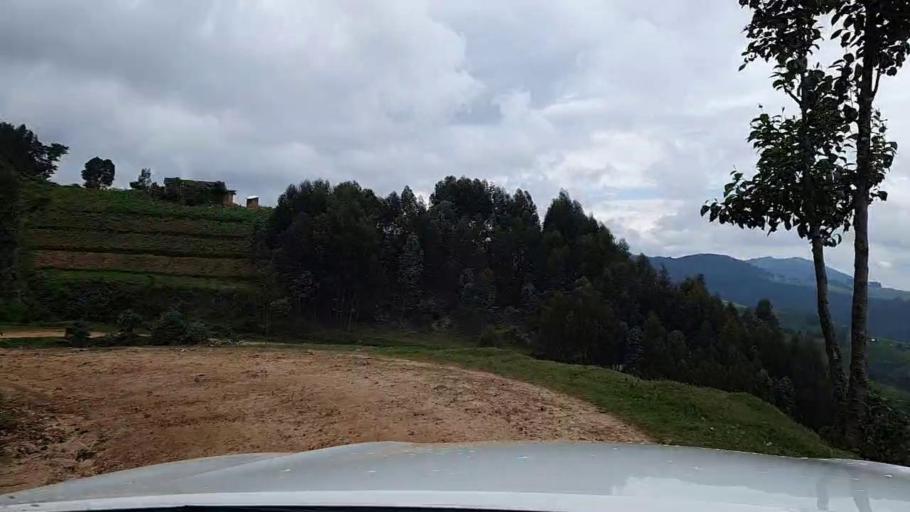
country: RW
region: Western Province
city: Kibuye
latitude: -2.2877
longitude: 29.3764
